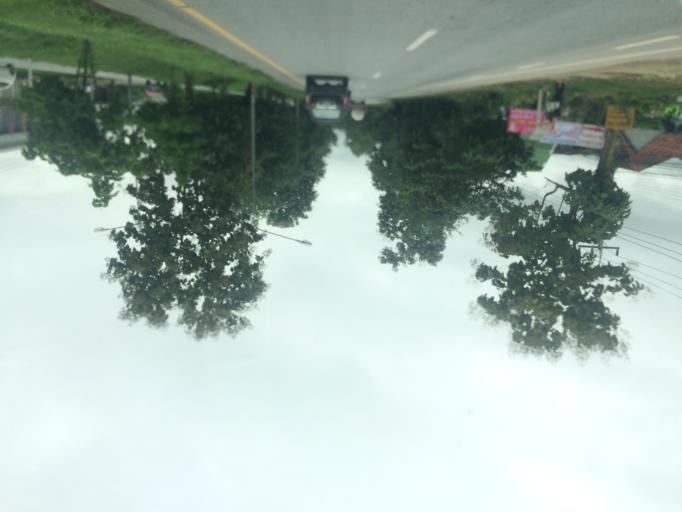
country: TH
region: Chiang Rai
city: Mae Lao
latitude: 19.7790
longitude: 99.7414
